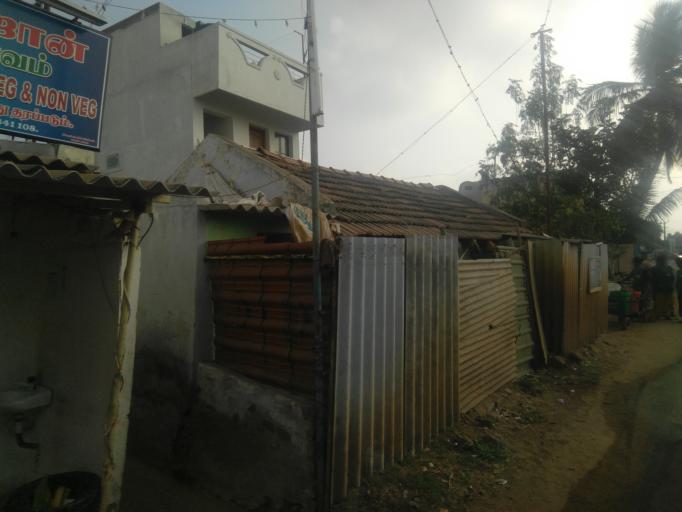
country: IN
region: Tamil Nadu
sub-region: Coimbatore
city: Coimbatore
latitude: 11.0650
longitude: 76.9108
